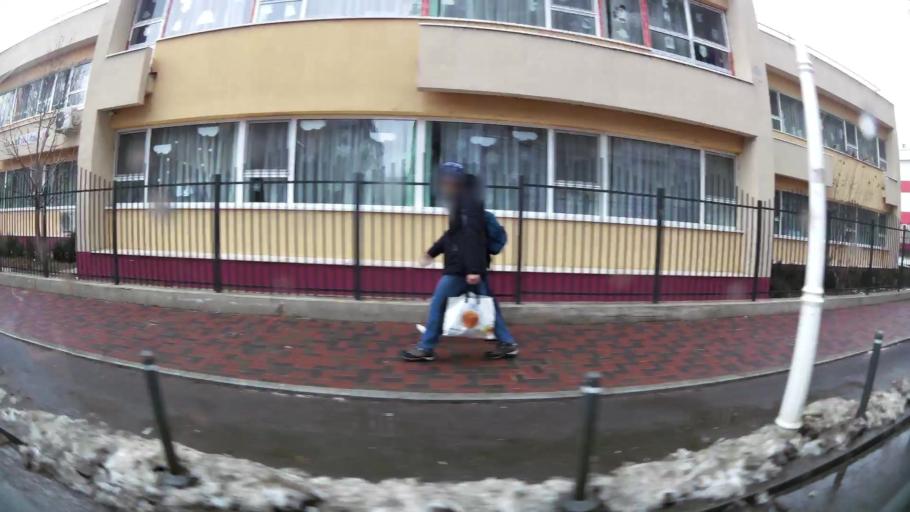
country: RO
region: Ilfov
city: Dobroesti
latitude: 44.4229
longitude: 26.1715
